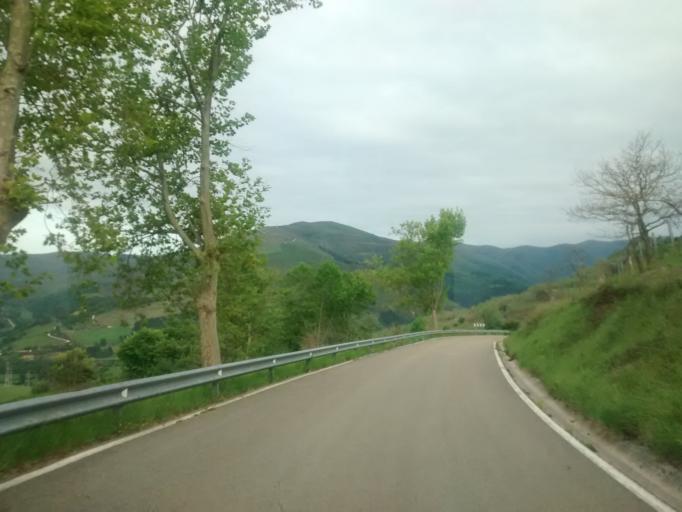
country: ES
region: Cantabria
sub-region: Provincia de Cantabria
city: San Vicente de la Barquera
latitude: 43.2513
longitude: -4.4279
